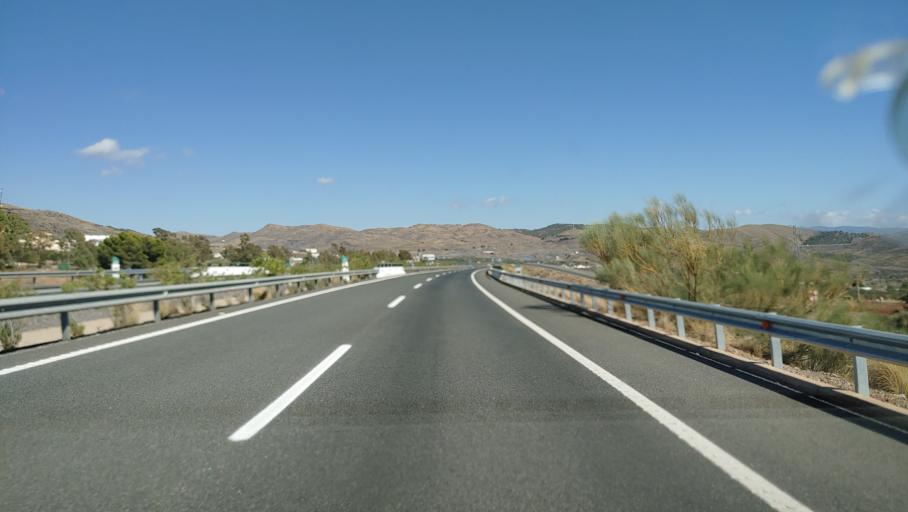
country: ES
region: Andalusia
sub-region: Provincia de Almeria
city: Gergal
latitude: 37.1169
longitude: -2.5525
